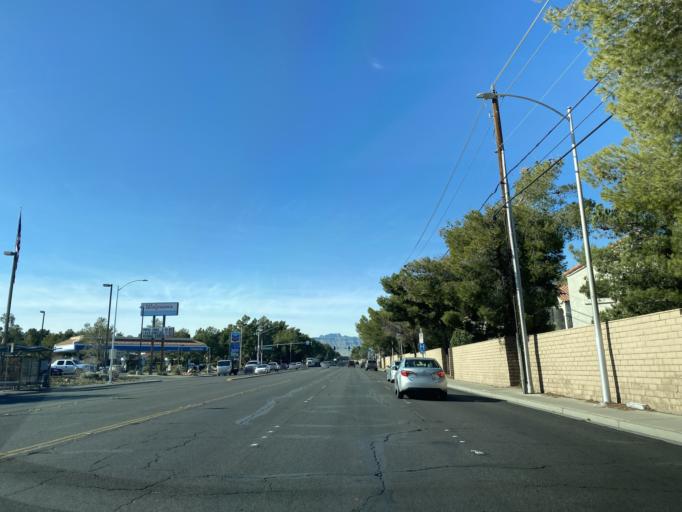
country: US
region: Nevada
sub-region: Clark County
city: Spring Valley
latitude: 36.0999
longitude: -115.2413
